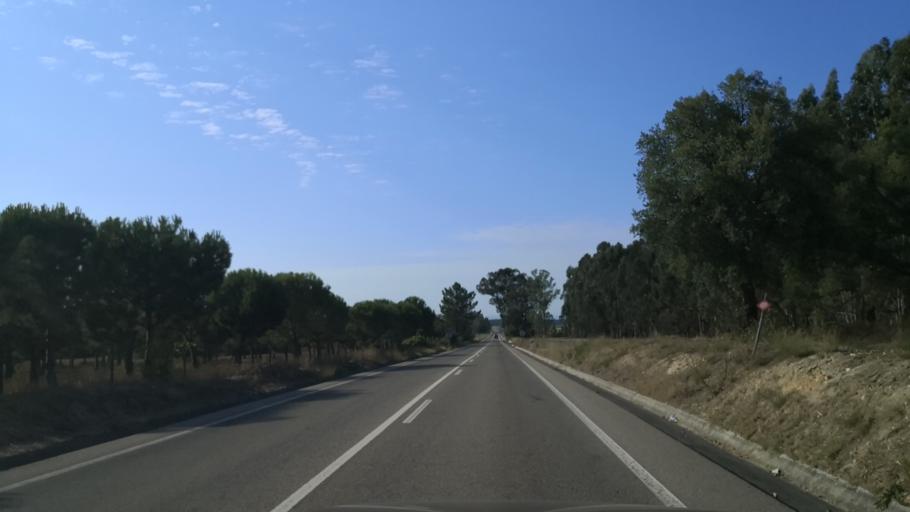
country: PT
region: Santarem
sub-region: Almeirim
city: Fazendas de Almeirim
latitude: 39.1431
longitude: -8.6139
